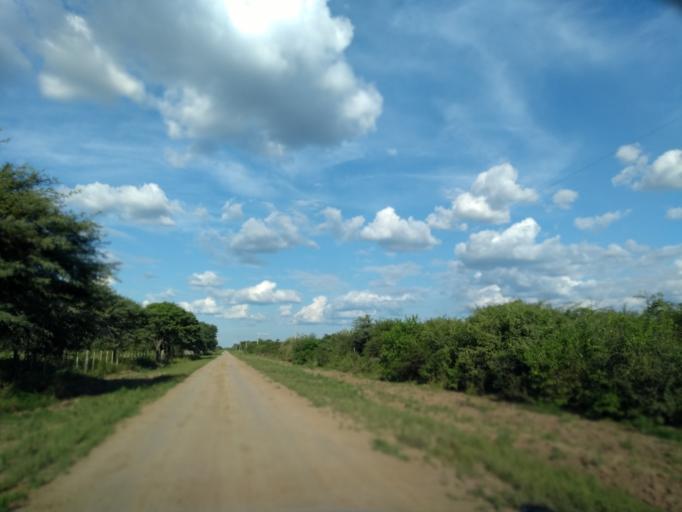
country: AR
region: Chaco
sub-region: Departamento de Quitilipi
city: Quitilipi
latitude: -26.7704
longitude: -60.2052
